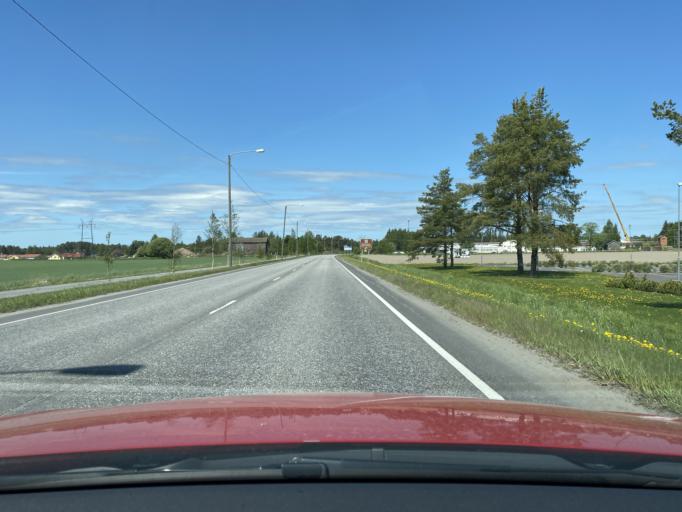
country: FI
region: Satakunta
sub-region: Rauma
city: Eura
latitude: 61.1214
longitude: 22.1353
